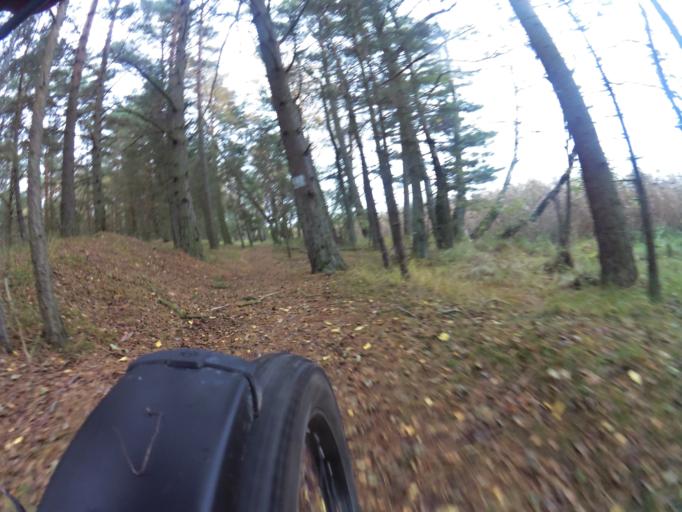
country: PL
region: Pomeranian Voivodeship
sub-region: Powiat leborski
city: Leba
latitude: 54.7731
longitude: 17.6482
